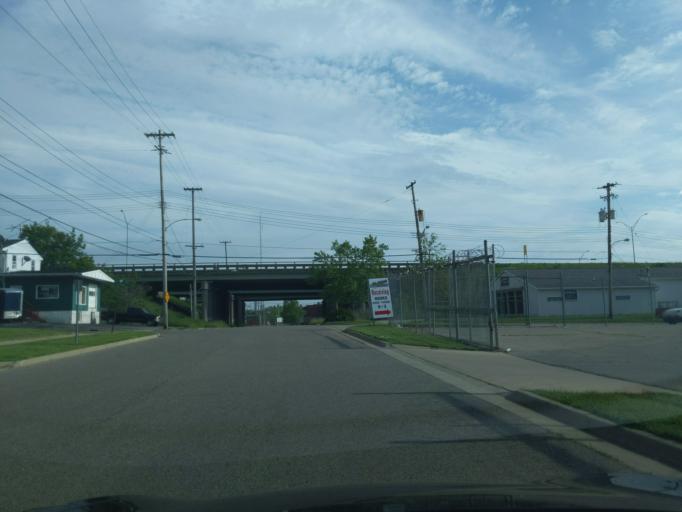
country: US
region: Michigan
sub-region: Ingham County
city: Lansing
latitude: 42.7267
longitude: -84.5412
